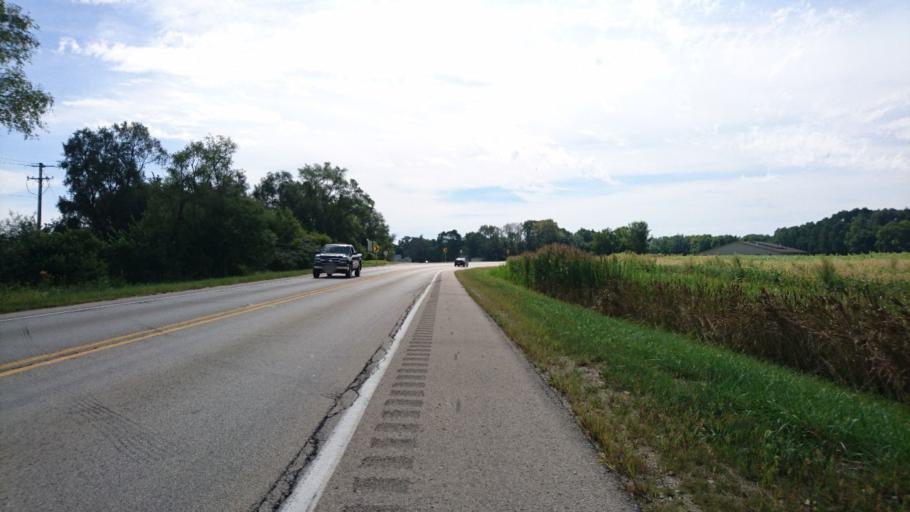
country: US
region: Illinois
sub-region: Will County
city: Wilmington
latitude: 41.3136
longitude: -88.1324
